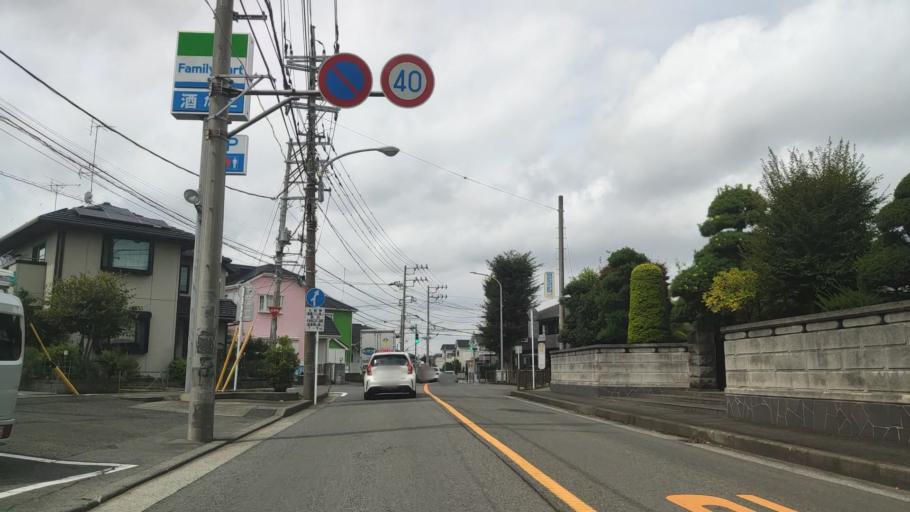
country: JP
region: Kanagawa
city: Minami-rinkan
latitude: 35.4720
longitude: 139.4893
